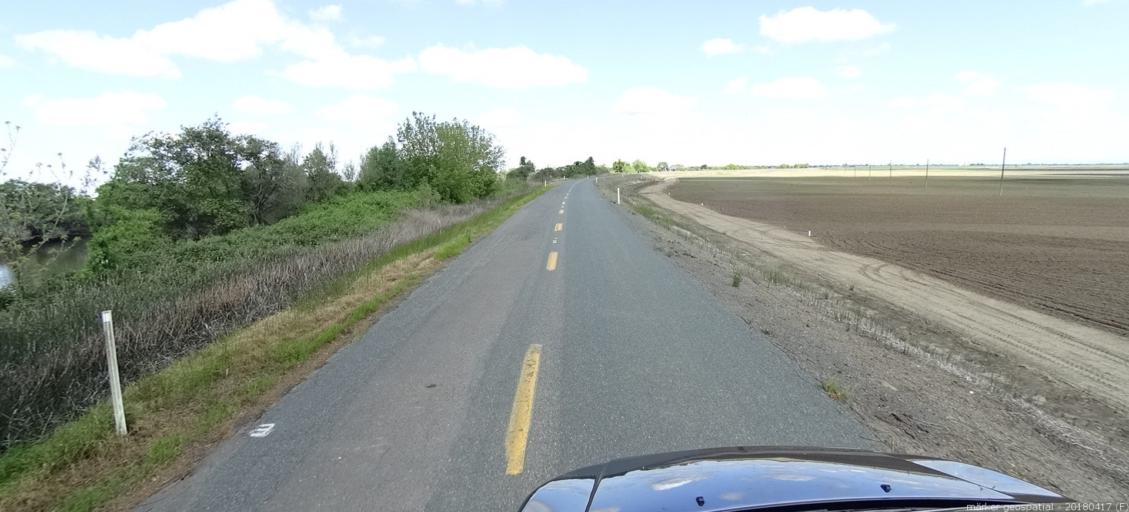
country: US
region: California
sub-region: Sacramento County
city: Walnut Grove
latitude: 38.1967
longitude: -121.5463
